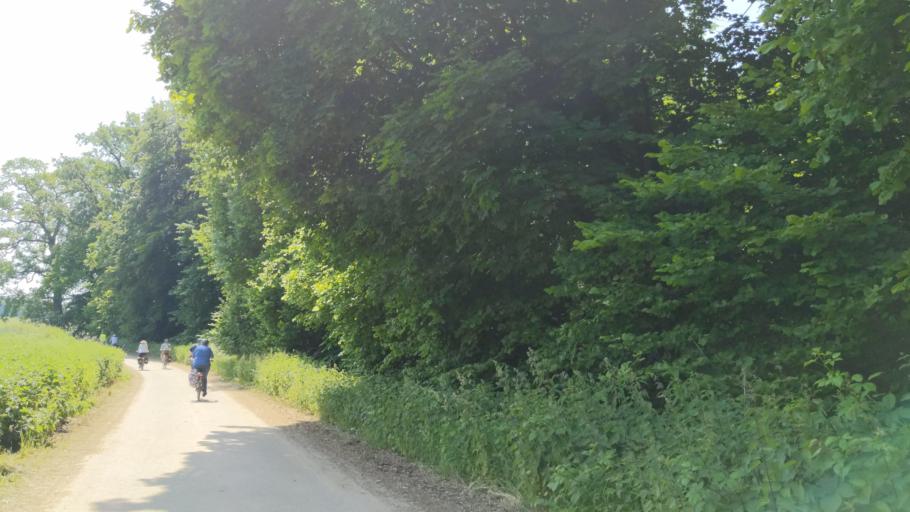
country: DE
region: Schleswig-Holstein
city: Behlendorf
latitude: 53.6912
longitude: 10.6735
